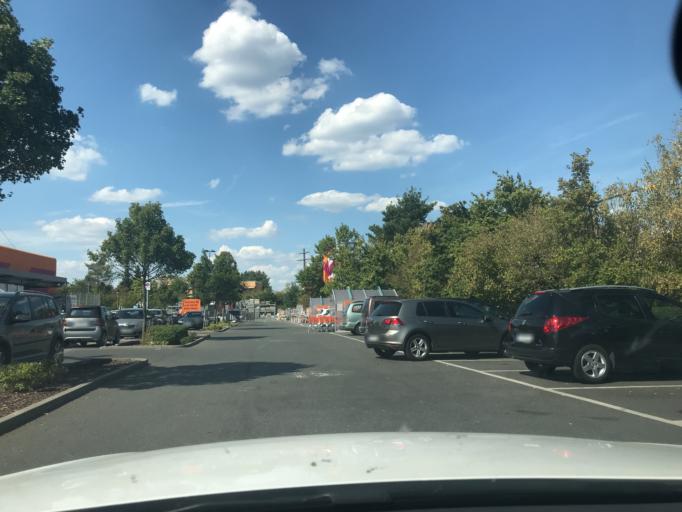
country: DE
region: Bavaria
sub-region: Regierungsbezirk Mittelfranken
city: Erlangen
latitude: 49.5775
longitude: 10.9657
